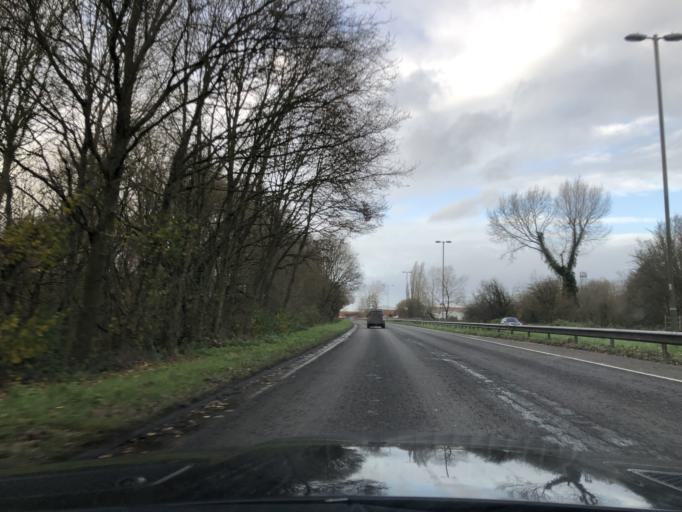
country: GB
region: England
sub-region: Surrey
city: Frimley
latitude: 51.3267
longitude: -0.7673
